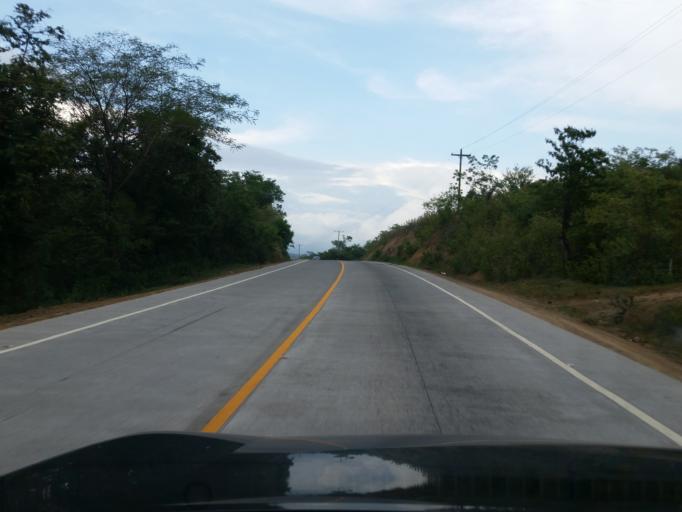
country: NI
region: Managua
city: Carlos Fonseca Amador
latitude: 12.0626
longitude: -86.4631
